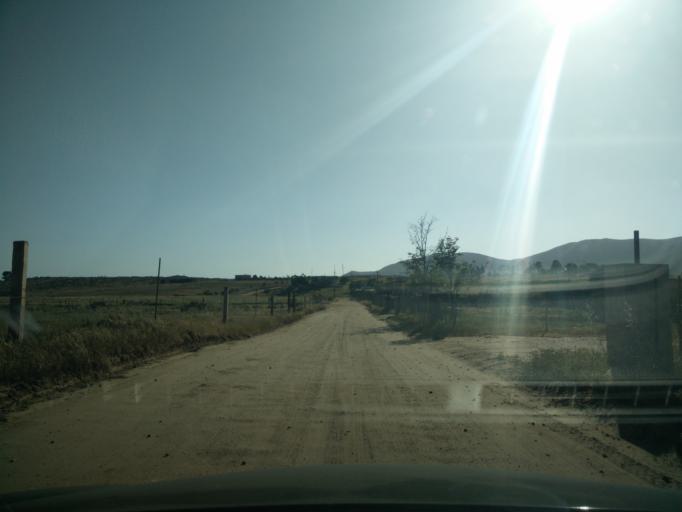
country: MX
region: Baja California
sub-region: Ensenada
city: Rancho Verde
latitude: 32.0472
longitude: -116.6472
